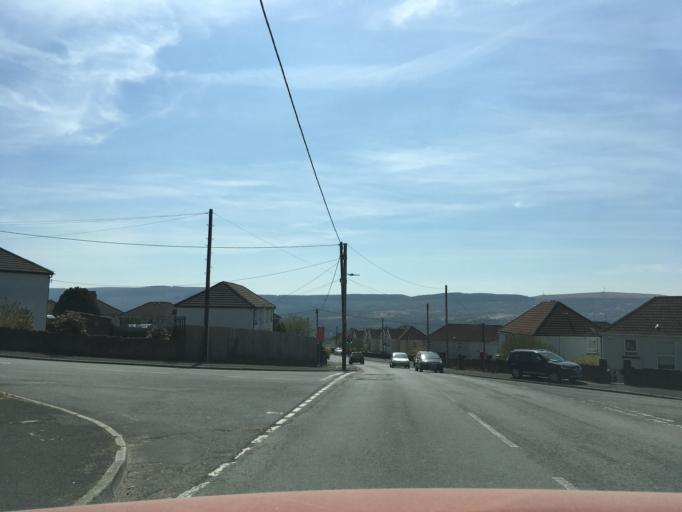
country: GB
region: Wales
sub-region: Merthyr Tydfil County Borough
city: Merthyr Tydfil
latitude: 51.7652
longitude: -3.3714
